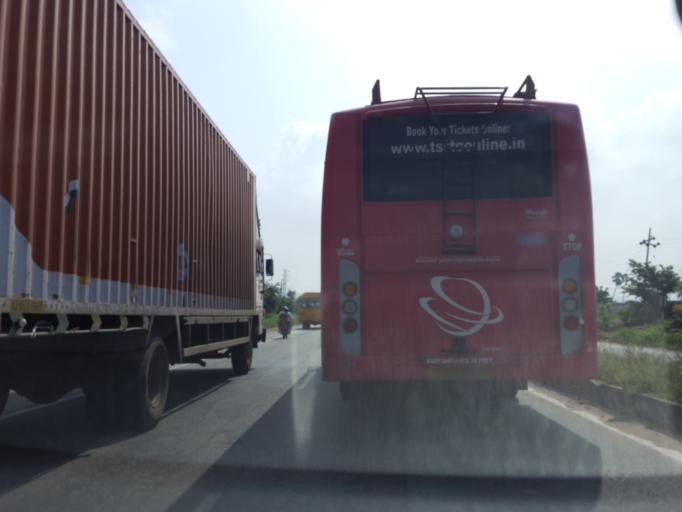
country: IN
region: Telangana
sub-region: Rangareddi
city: Ghatkesar
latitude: 17.3046
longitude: 78.7316
